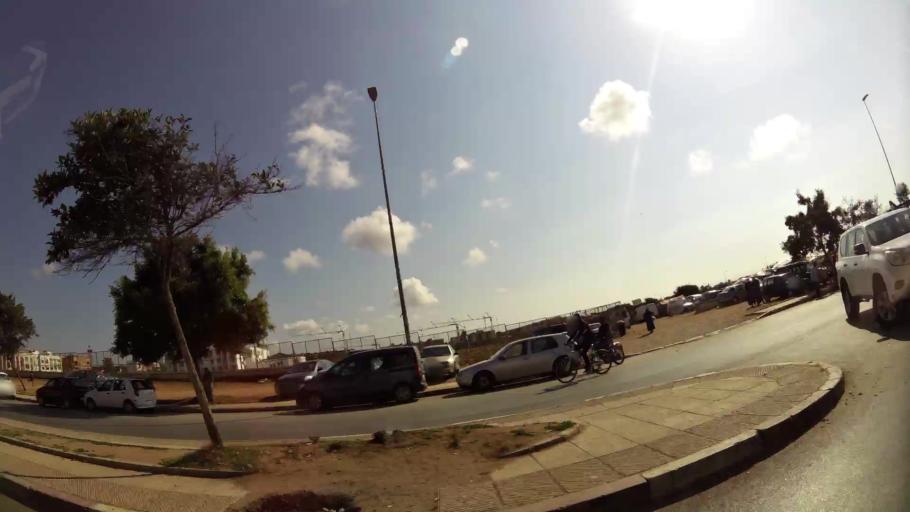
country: MA
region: Rabat-Sale-Zemmour-Zaer
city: Sale
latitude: 34.0496
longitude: -6.7884
